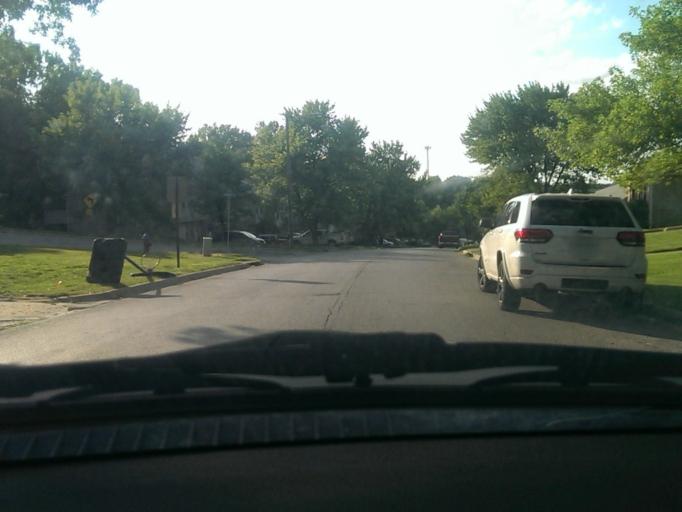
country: US
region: Kansas
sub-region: Johnson County
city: Westwood
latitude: 39.0663
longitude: -94.6087
